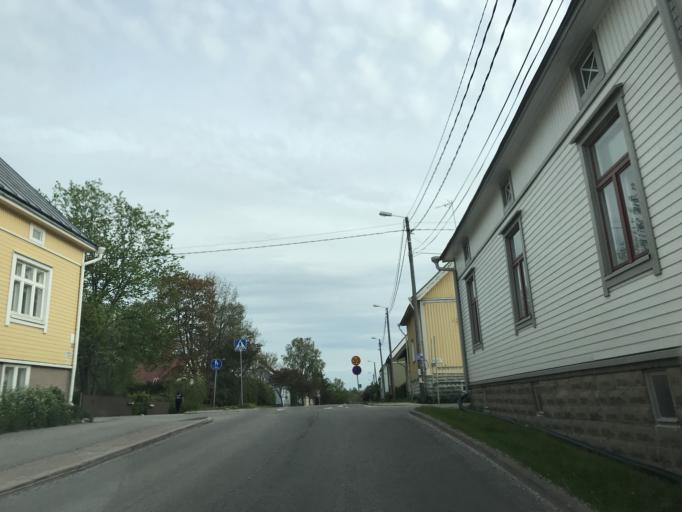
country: FI
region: Varsinais-Suomi
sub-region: Turku
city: Turku
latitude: 60.4538
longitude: 22.3077
